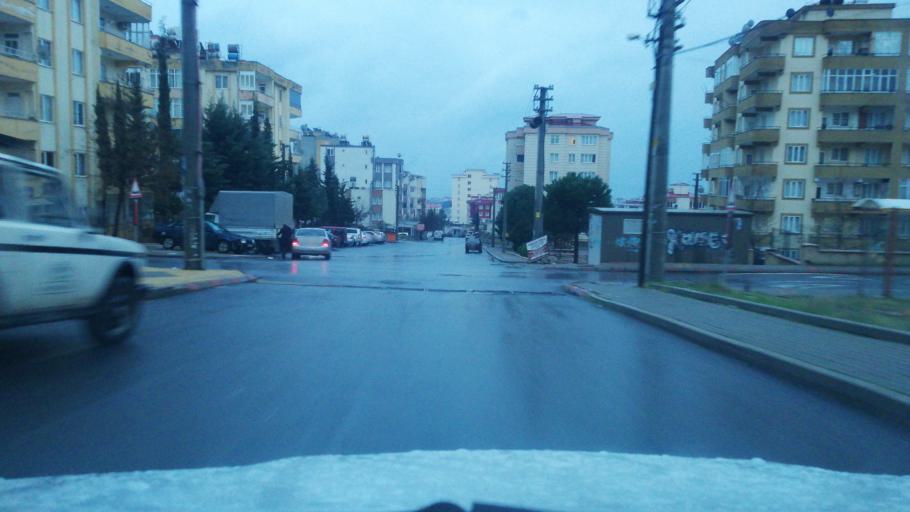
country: TR
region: Kahramanmaras
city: Kahramanmaras
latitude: 37.5960
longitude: 36.8991
